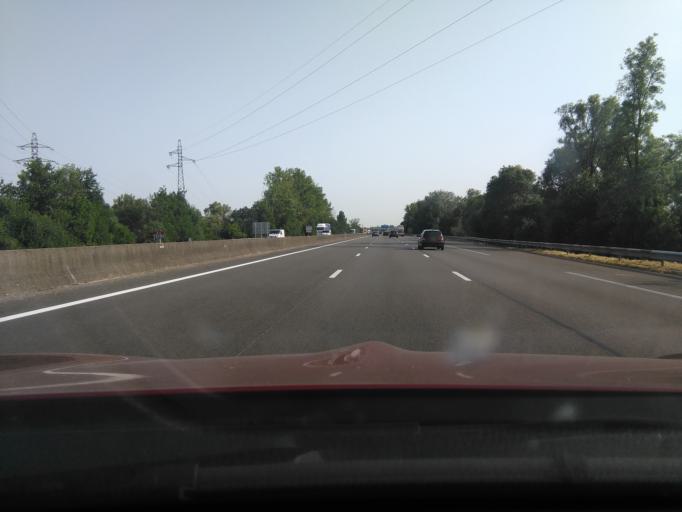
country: FR
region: Rhone-Alpes
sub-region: Departement du Rhone
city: Arnas
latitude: 46.0313
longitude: 4.7254
